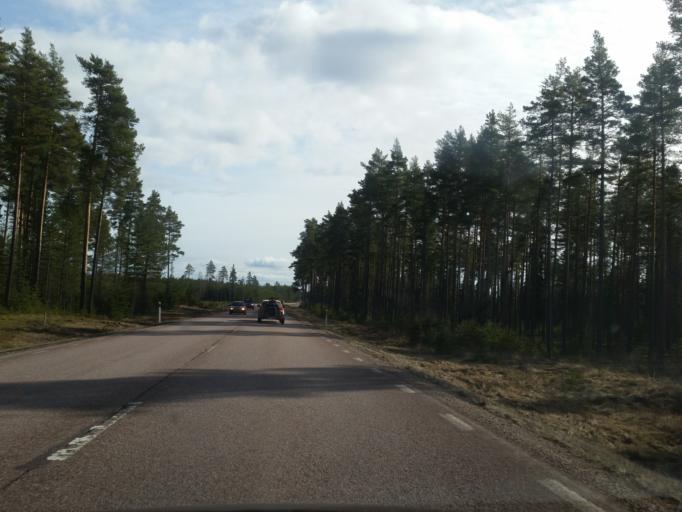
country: SE
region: Dalarna
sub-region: Mora Kommun
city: Mora
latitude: 60.9814
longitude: 14.6896
